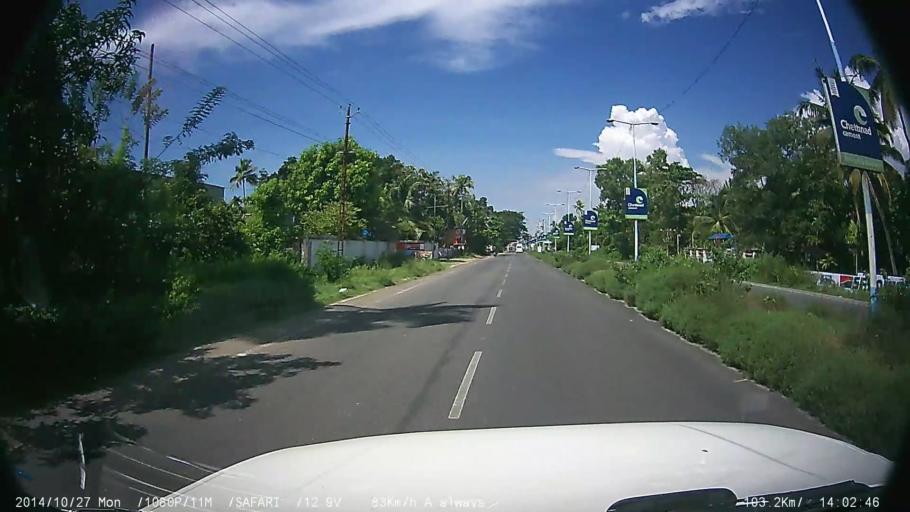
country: IN
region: Kerala
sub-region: Alappuzha
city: Vayalar
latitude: 9.7133
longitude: 76.3171
